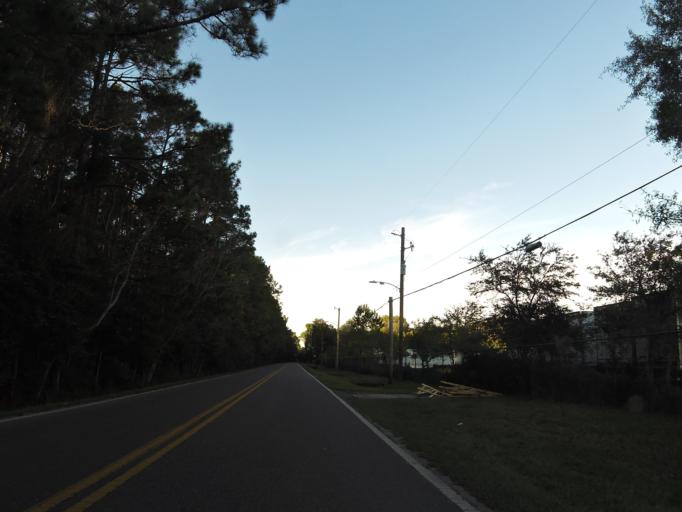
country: US
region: Florida
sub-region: Duval County
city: Jacksonville
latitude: 30.3571
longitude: -81.7647
